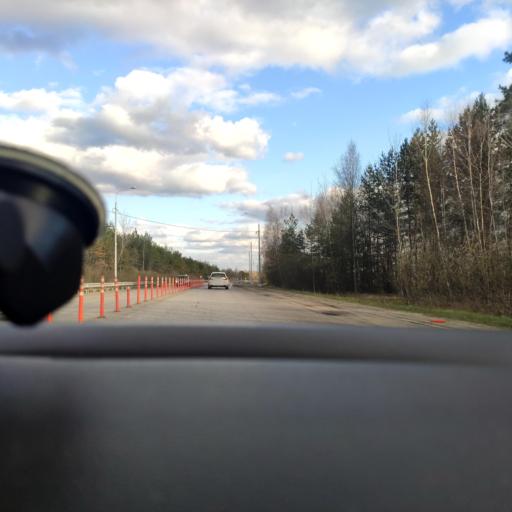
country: RU
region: Moskovskaya
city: Yegor'yevsk
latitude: 55.4471
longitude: 39.0114
